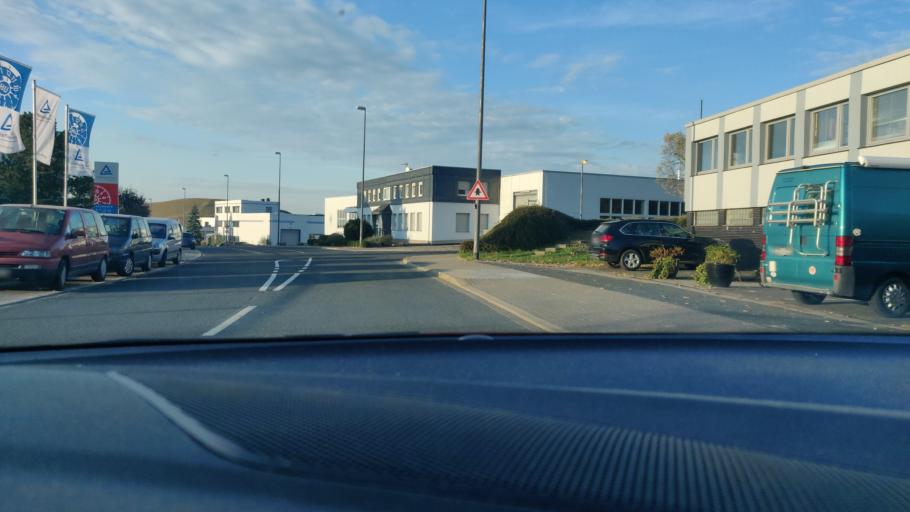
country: DE
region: North Rhine-Westphalia
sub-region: Regierungsbezirk Dusseldorf
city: Velbert
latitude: 51.3477
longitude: 7.0684
